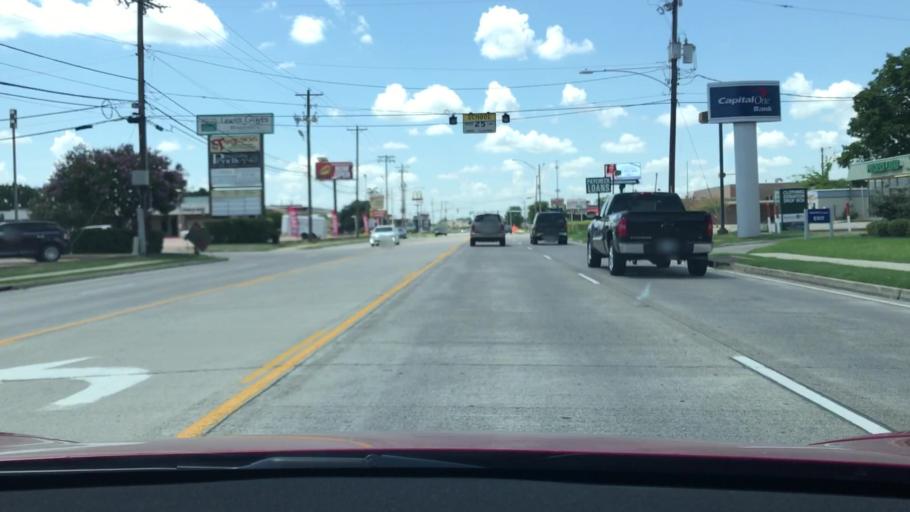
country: US
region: Louisiana
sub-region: Bossier Parish
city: Bossier City
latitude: 32.4552
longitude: -93.7222
